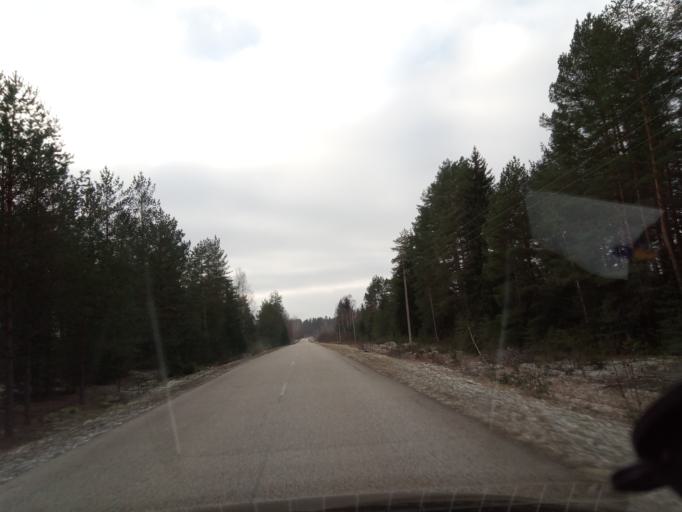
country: LT
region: Alytaus apskritis
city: Varena
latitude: 54.0270
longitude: 24.3532
